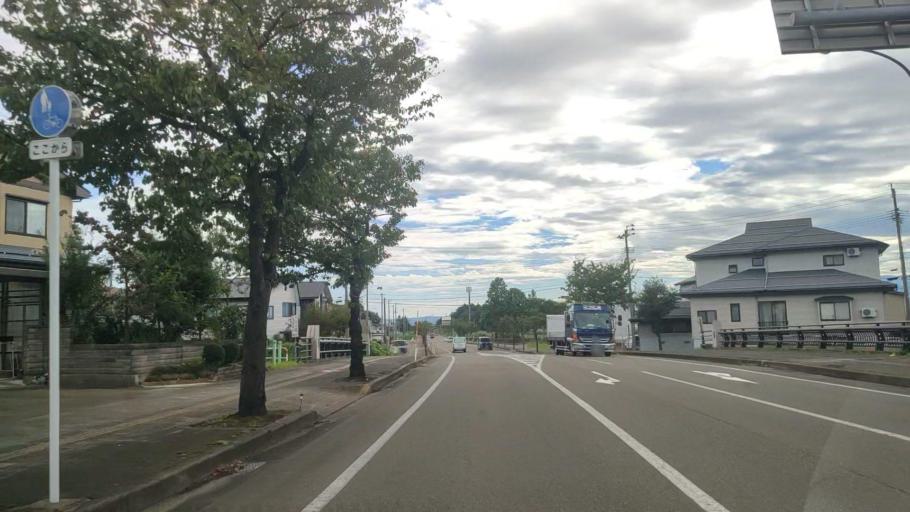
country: JP
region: Niigata
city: Joetsu
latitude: 37.0922
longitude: 138.2403
